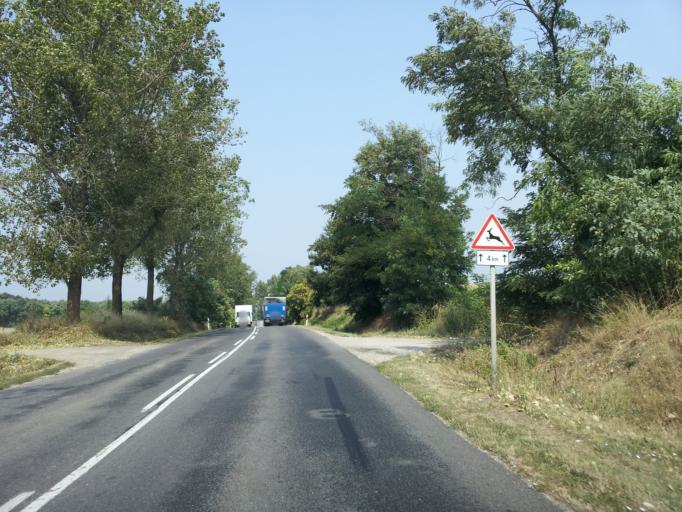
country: HU
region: Gyor-Moson-Sopron
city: Pannonhalma
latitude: 47.4844
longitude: 17.7858
